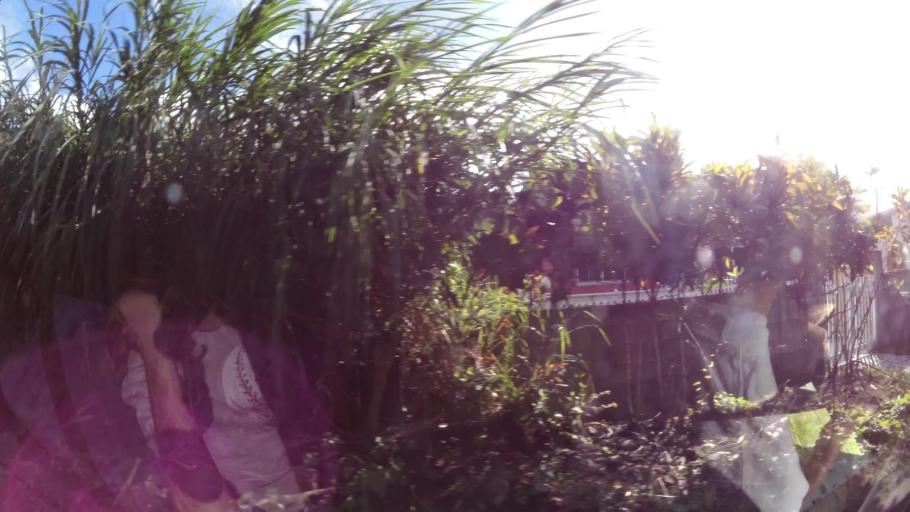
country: DM
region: Saint George
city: Roseau
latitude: 15.3032
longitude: -61.3775
